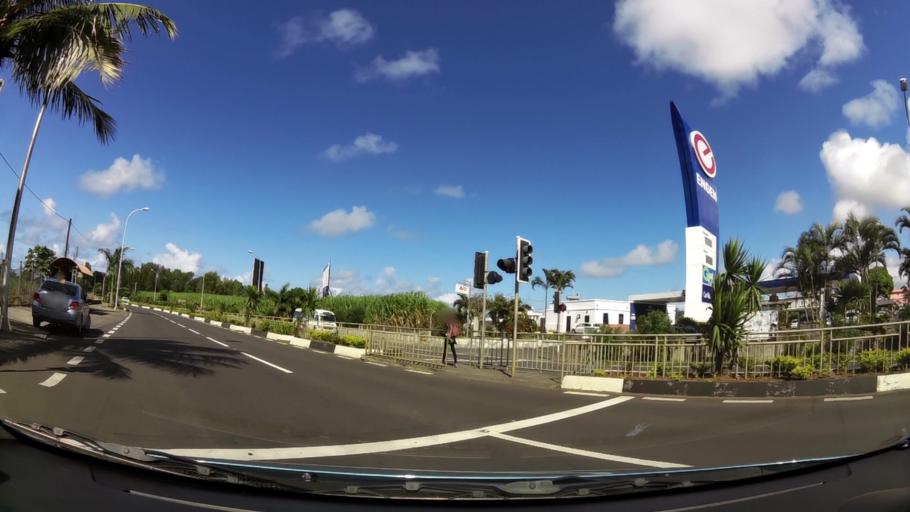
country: MU
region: Grand Port
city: Plaine Magnien
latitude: -20.4305
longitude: 57.6670
